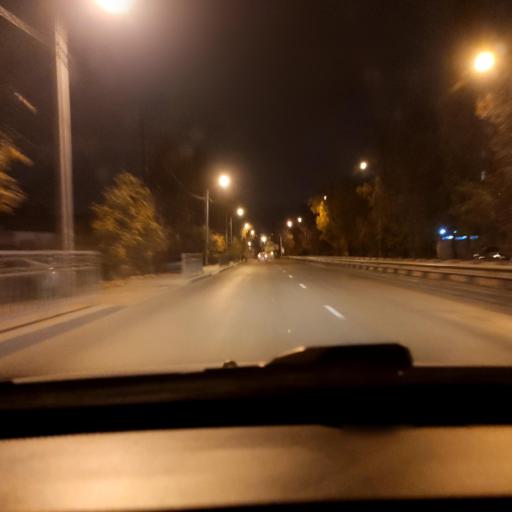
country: RU
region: Voronezj
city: Voronezh
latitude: 51.7039
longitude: 39.2298
